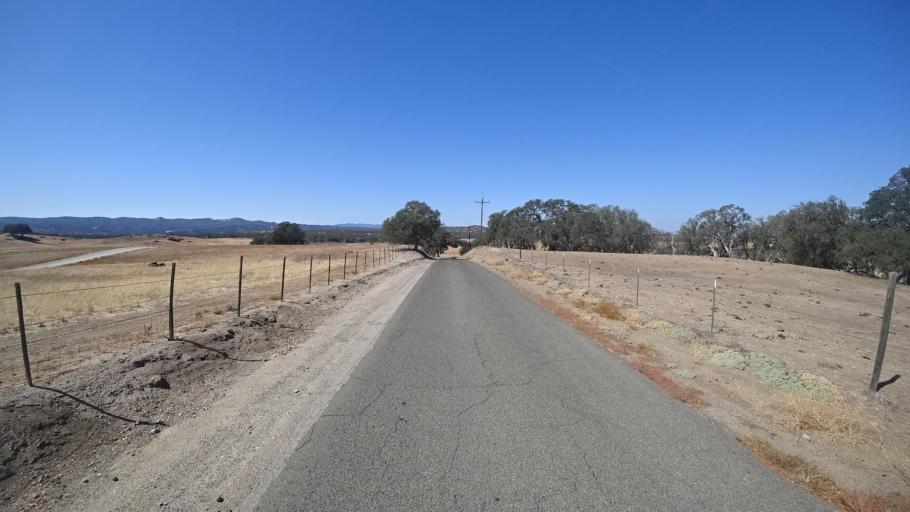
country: US
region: California
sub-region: San Luis Obispo County
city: Lake Nacimiento
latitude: 35.9084
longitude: -121.0363
